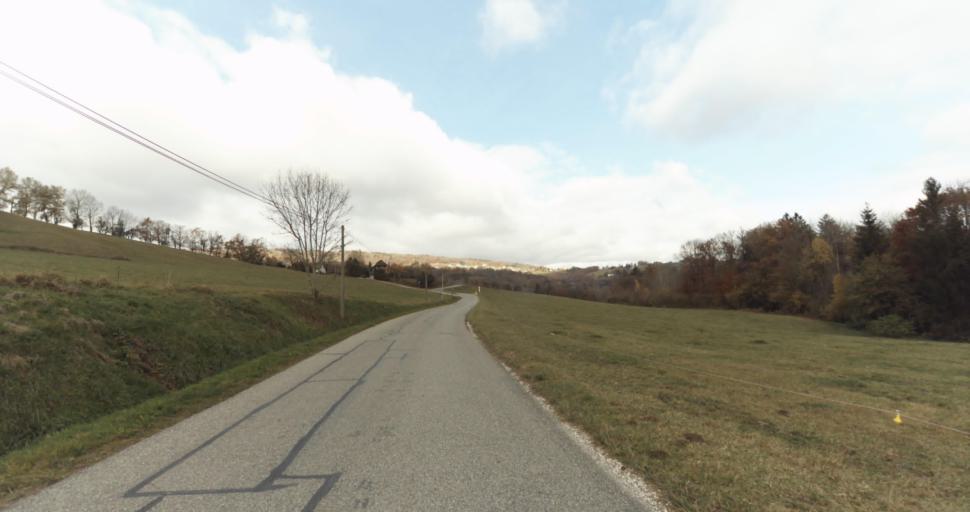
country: FR
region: Rhone-Alpes
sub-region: Departement de la Haute-Savoie
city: Epagny
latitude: 45.9607
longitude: 6.1035
